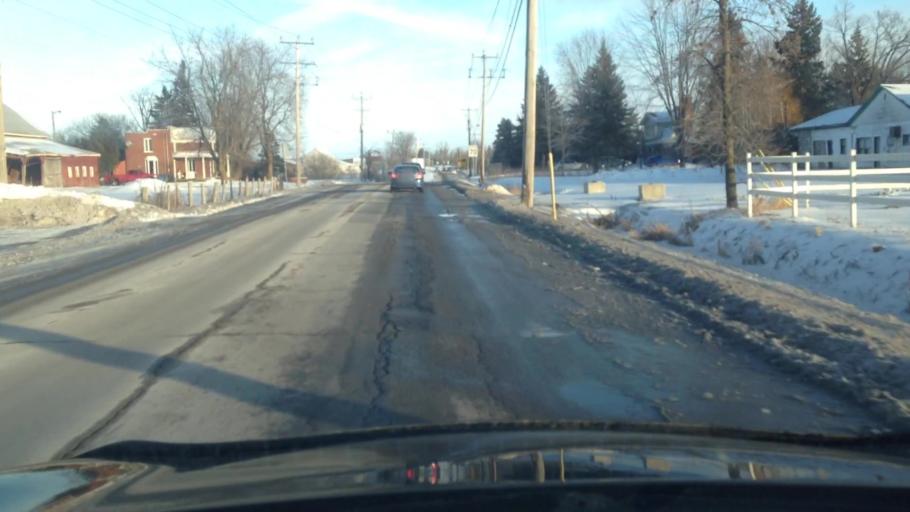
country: CA
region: Quebec
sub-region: Lanaudiere
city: Saint-Lin-Laurentides
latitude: 45.8521
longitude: -73.7770
